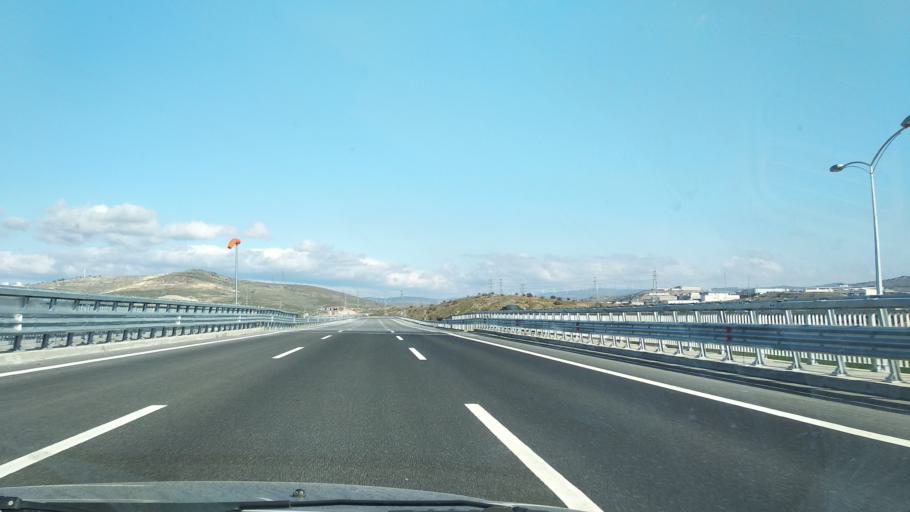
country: TR
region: Izmir
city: Aliaga
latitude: 38.8127
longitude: 27.0238
